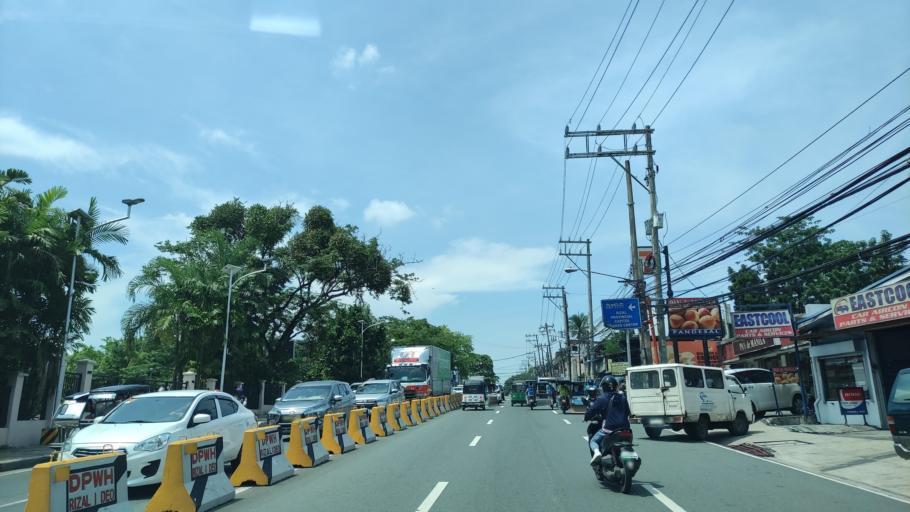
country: PH
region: Calabarzon
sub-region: Province of Rizal
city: Taytay
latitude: 14.5860
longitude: 121.1687
